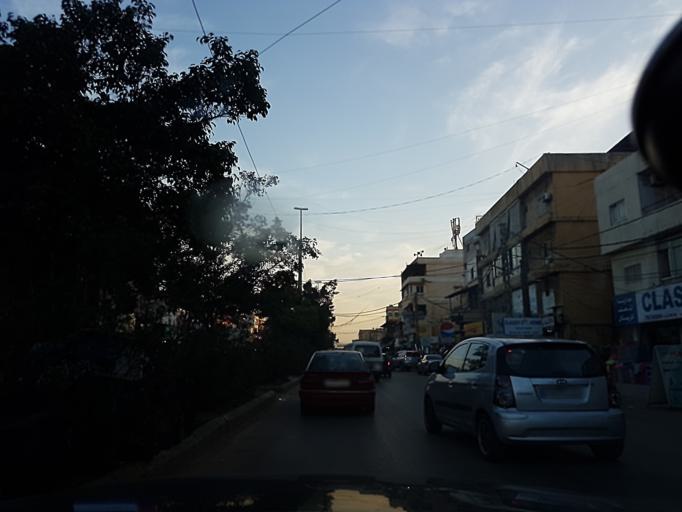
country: LB
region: Beyrouth
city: Beirut
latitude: 33.8365
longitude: 35.4846
